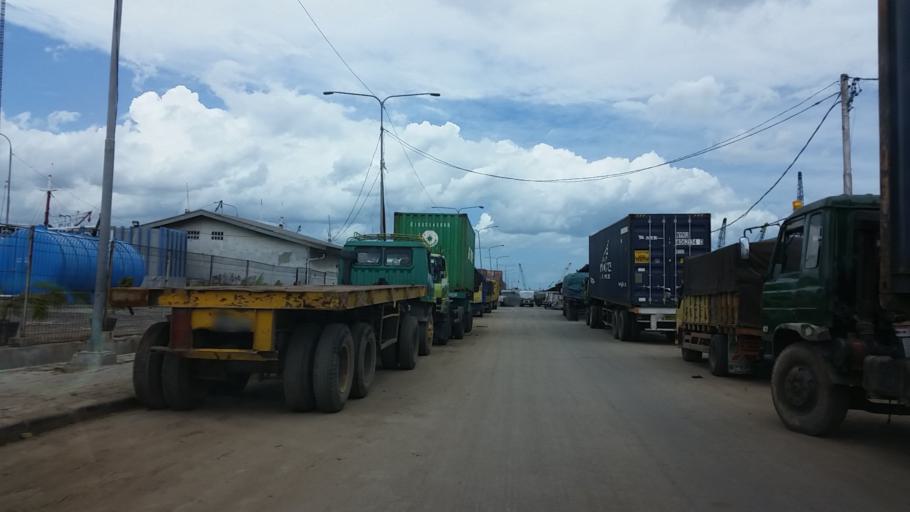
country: ID
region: Jakarta Raya
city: Jakarta
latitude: -6.1207
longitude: 106.8092
